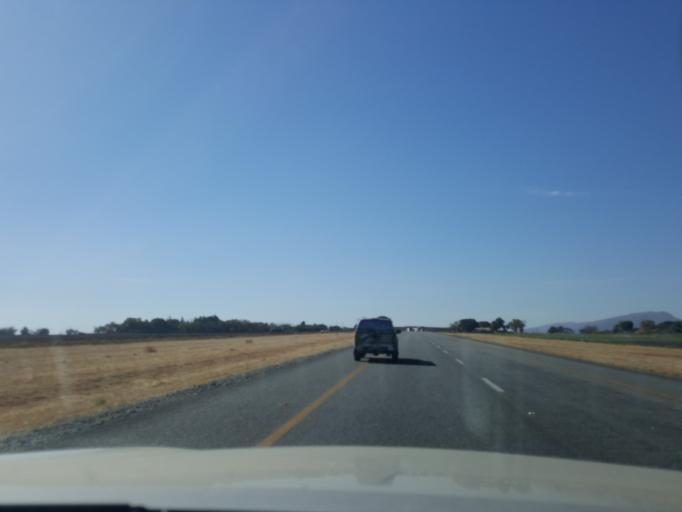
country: ZA
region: North-West
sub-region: Bojanala Platinum District Municipality
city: Brits
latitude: -25.6806
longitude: 27.8094
